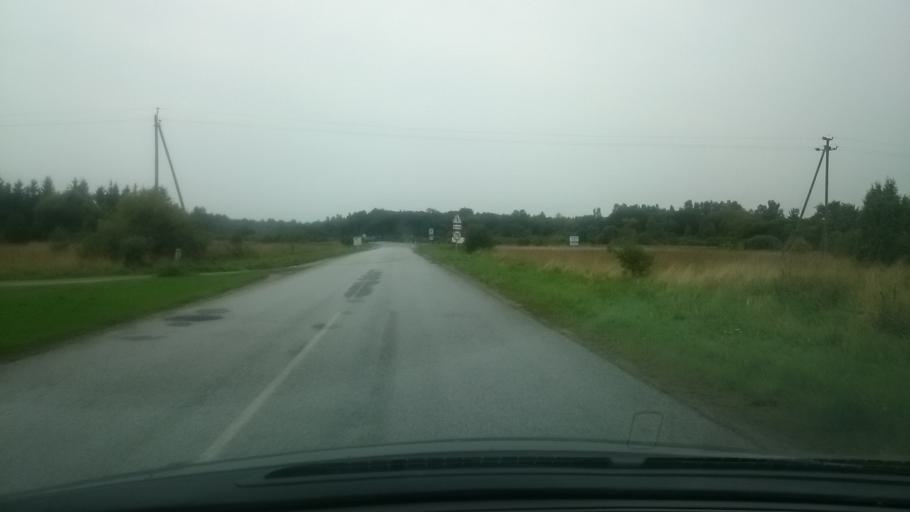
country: EE
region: Harju
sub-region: Raasiku vald
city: Raasiku
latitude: 59.4538
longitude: 25.2023
